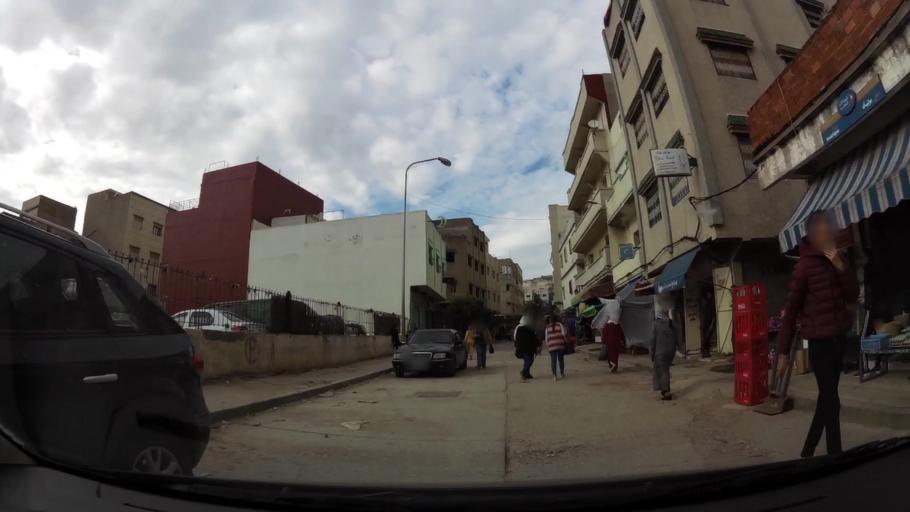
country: MA
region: Tanger-Tetouan
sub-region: Tanger-Assilah
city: Tangier
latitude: 35.7599
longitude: -5.7912
